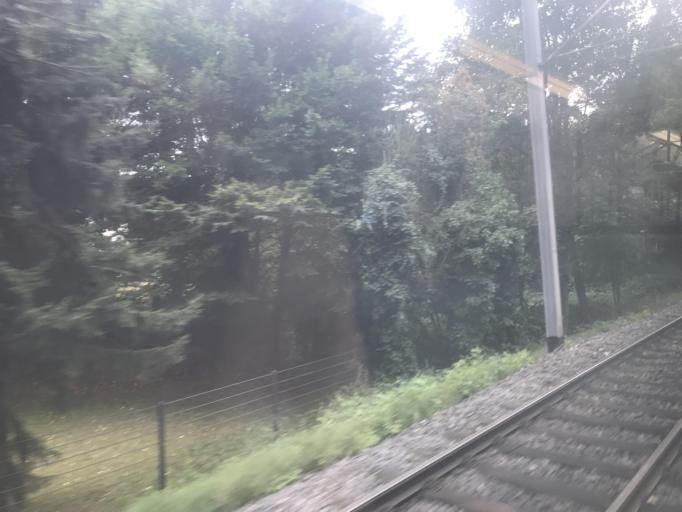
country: DE
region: North Rhine-Westphalia
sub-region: Regierungsbezirk Koln
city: Konigswinter
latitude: 50.7137
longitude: 7.1693
